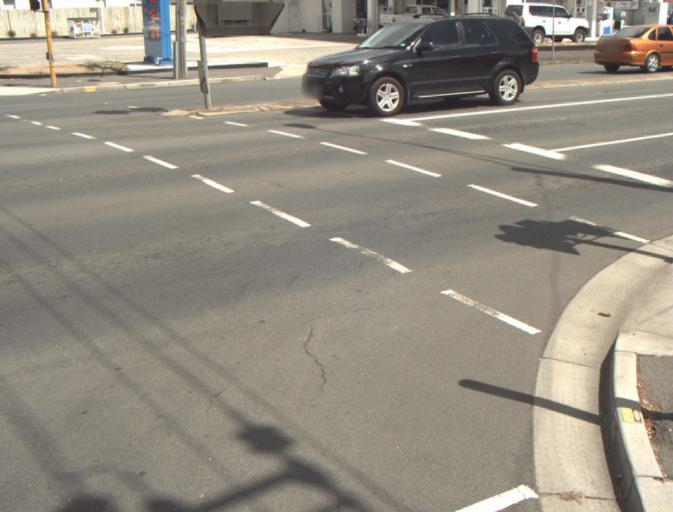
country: AU
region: Tasmania
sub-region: Launceston
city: Launceston
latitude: -41.4242
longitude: 147.1367
